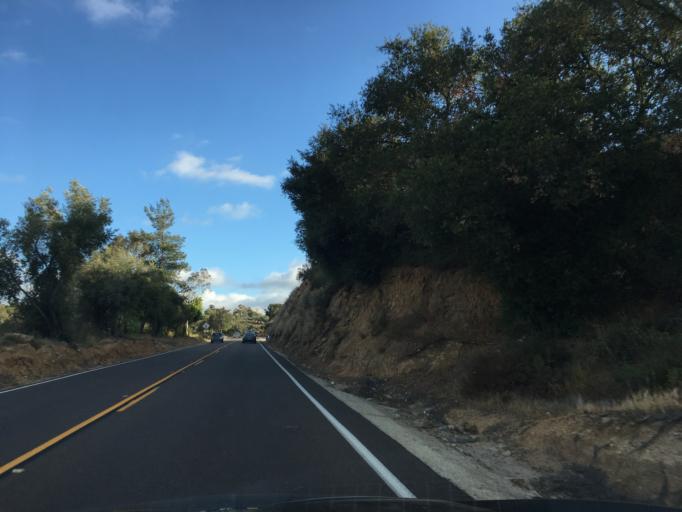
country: US
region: California
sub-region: San Diego County
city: Valley Center
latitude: 33.2450
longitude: -117.0543
